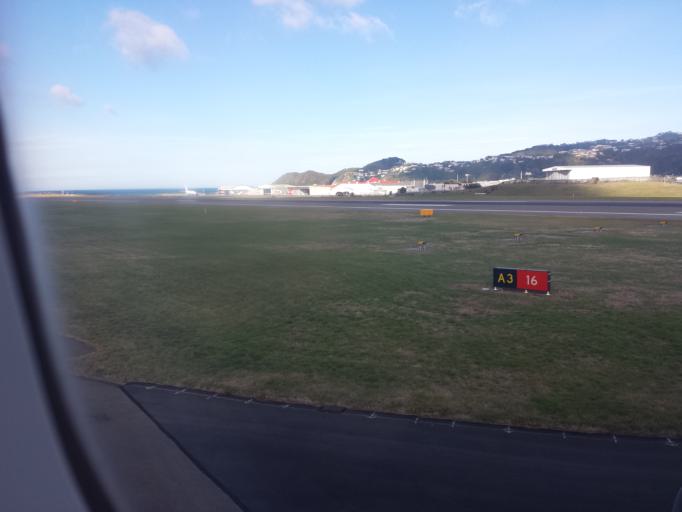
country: NZ
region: Wellington
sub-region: Wellington City
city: Wellington
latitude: -41.3218
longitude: 174.8084
